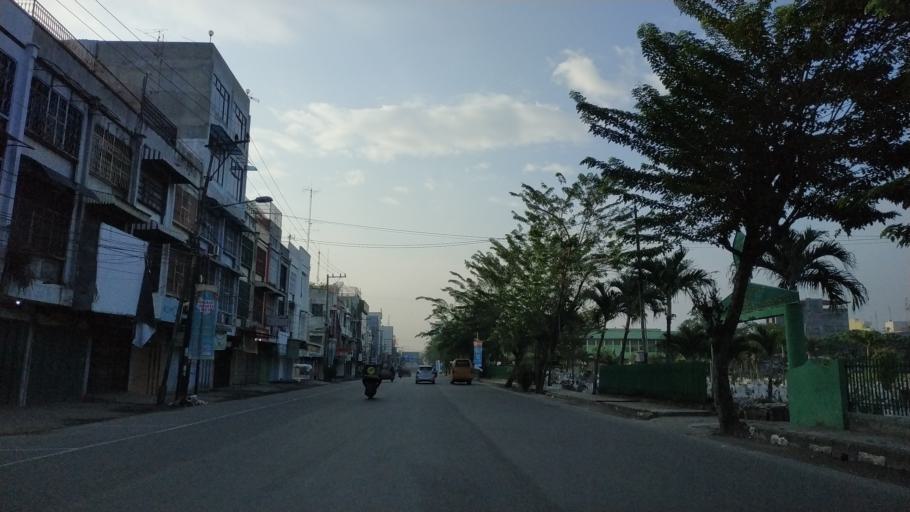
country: ID
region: North Sumatra
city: Medan
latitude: 3.5915
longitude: 98.6894
